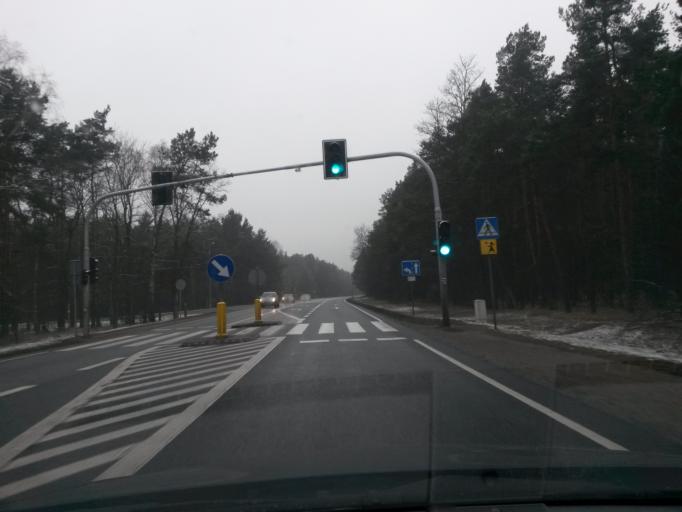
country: PL
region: Kujawsko-Pomorskie
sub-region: Powiat torunski
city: Wielka Nieszawka
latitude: 52.9839
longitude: 18.4875
